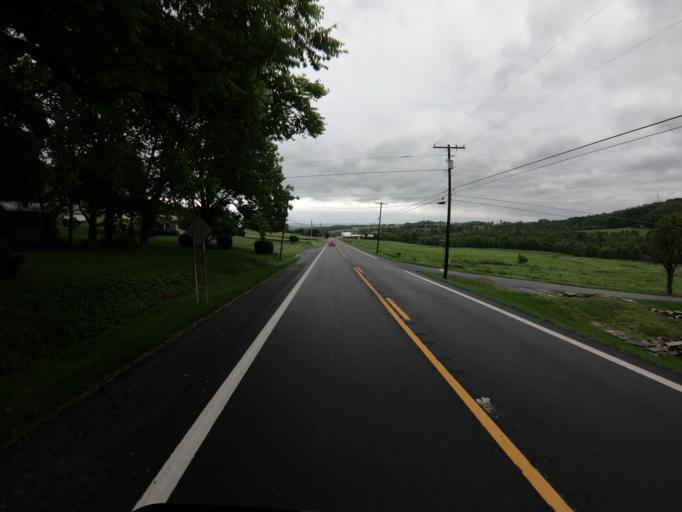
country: US
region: Maryland
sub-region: Frederick County
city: Myersville
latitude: 39.4755
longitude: -77.6064
